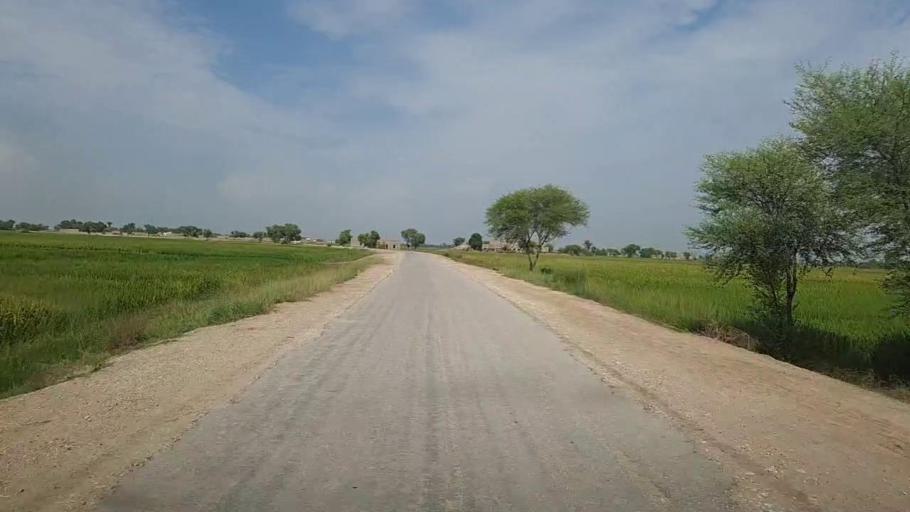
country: PK
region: Sindh
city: Thul
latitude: 28.2622
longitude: 68.8151
